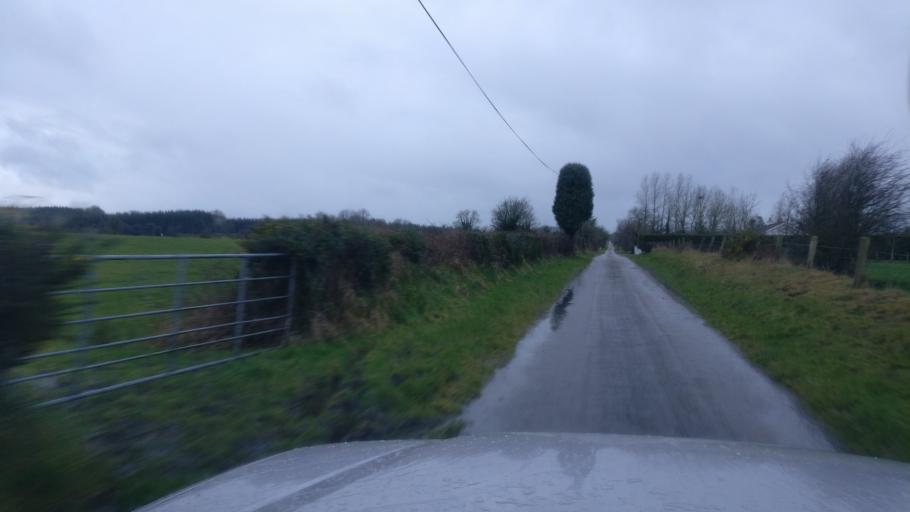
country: IE
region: Connaught
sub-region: County Galway
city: Ballinasloe
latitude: 53.2762
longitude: -8.3152
